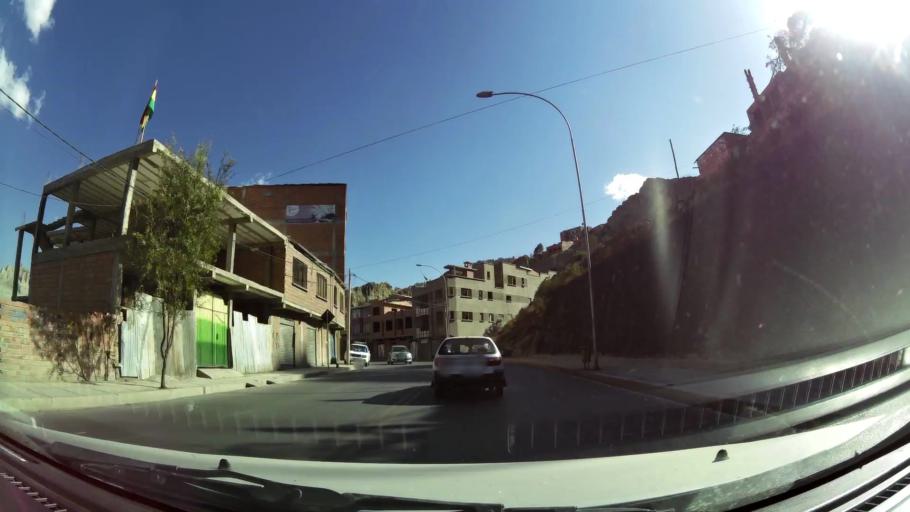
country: BO
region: La Paz
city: La Paz
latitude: -16.5180
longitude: -68.1232
